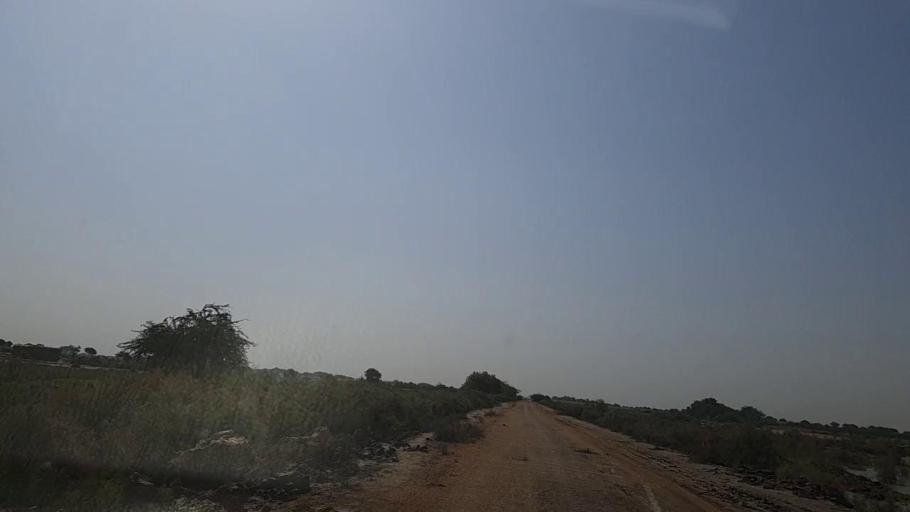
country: PK
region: Sindh
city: Daro Mehar
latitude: 24.7017
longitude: 68.1282
